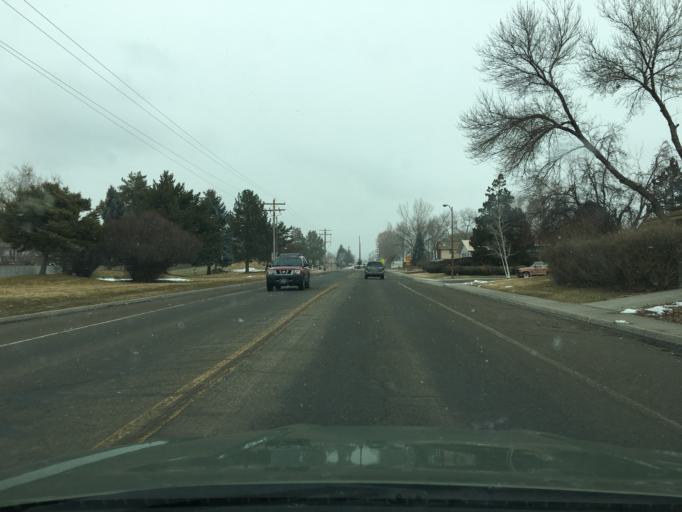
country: US
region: Colorado
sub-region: Montrose County
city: Montrose
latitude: 38.4729
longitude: -107.8566
